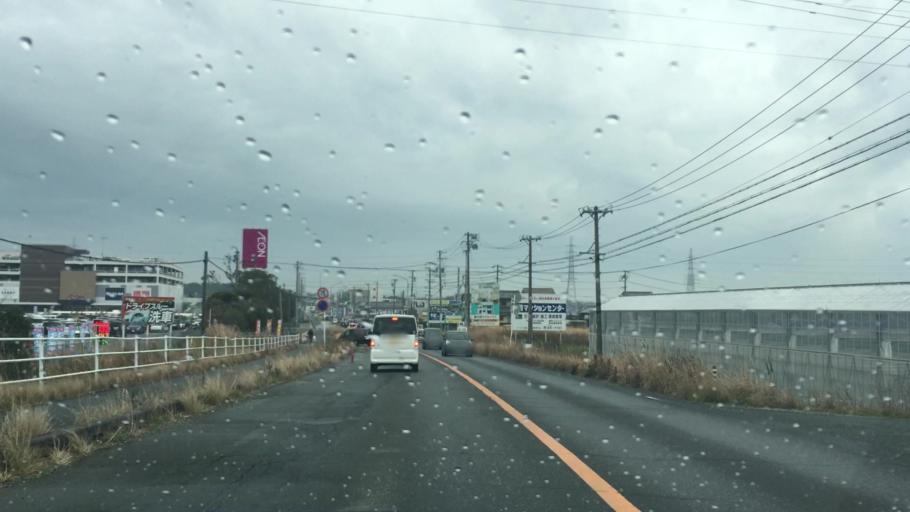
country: JP
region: Aichi
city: Toyohashi
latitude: 34.7119
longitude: 137.3865
